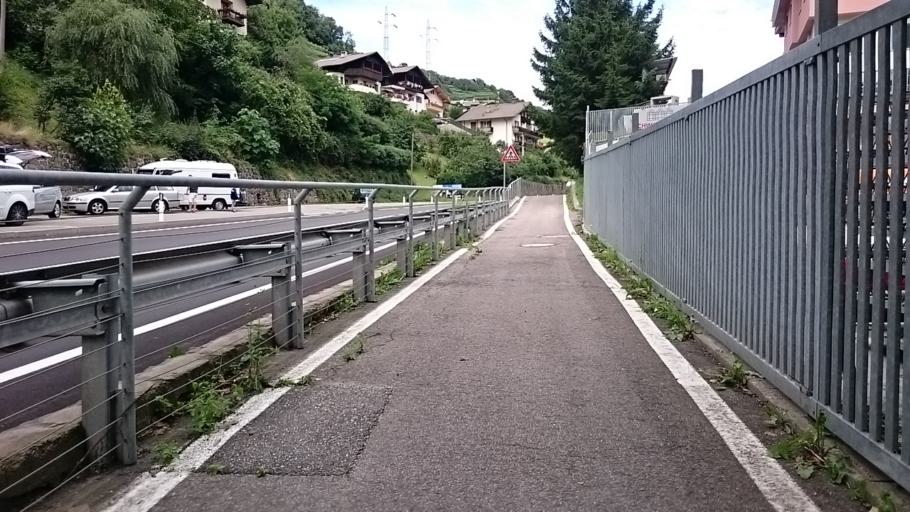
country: IT
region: Trentino-Alto Adige
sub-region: Bolzano
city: Ponte Gardena
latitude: 46.5880
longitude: 11.5241
